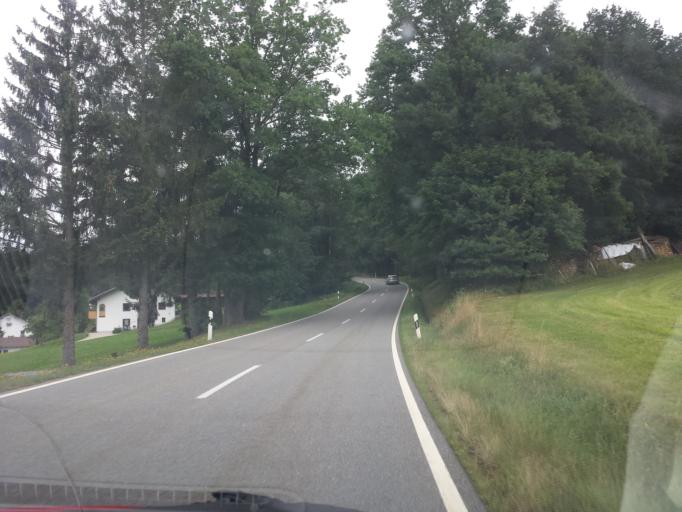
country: DE
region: Bavaria
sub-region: Lower Bavaria
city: Viechtach
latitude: 49.1073
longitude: 12.8838
